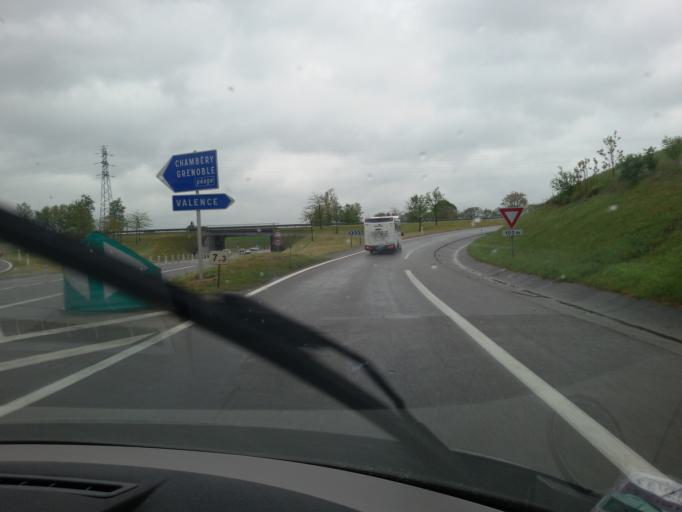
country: FR
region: Rhone-Alpes
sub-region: Departement de la Drome
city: Bourg-de-Peage
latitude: 45.0252
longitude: 5.0810
